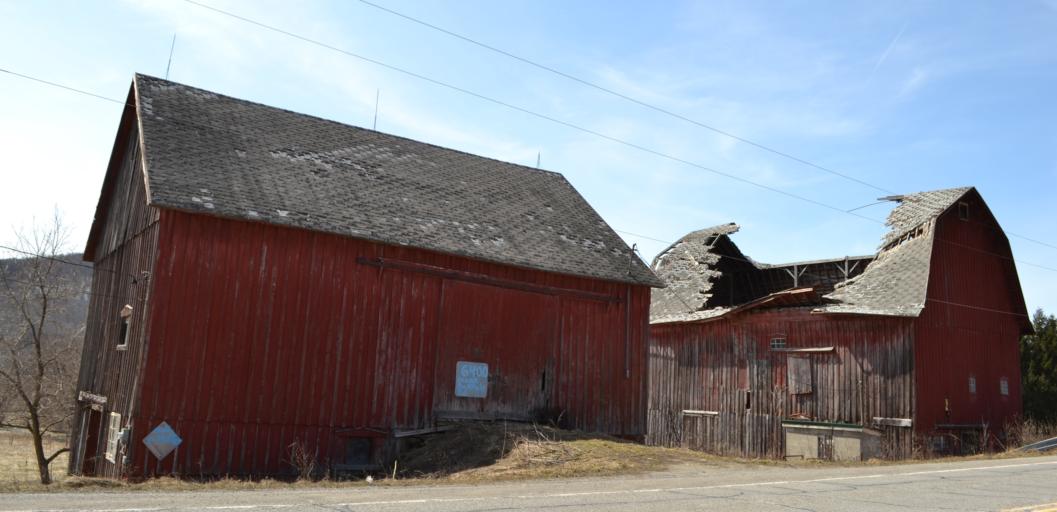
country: US
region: New York
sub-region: Cattaraugus County
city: Franklinville
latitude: 42.2767
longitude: -78.4482
